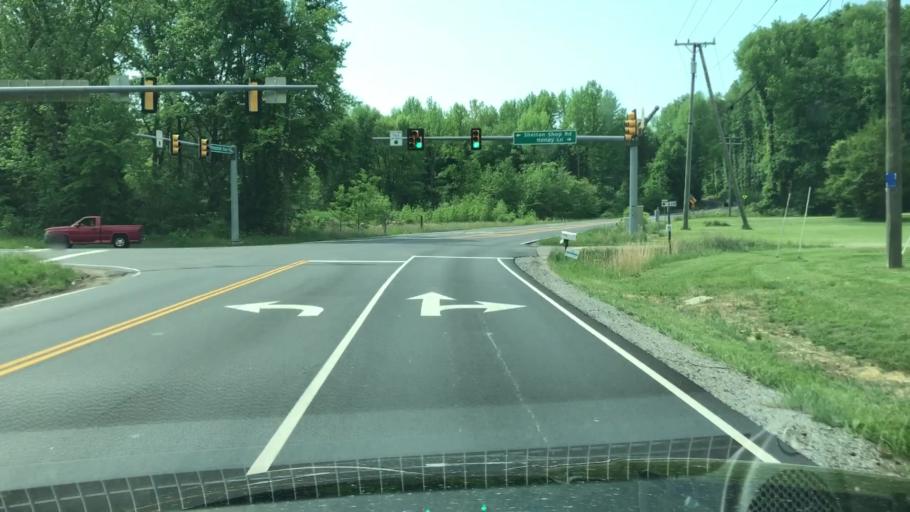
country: US
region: Virginia
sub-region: Stafford County
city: Stafford
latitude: 38.4513
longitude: -77.4889
